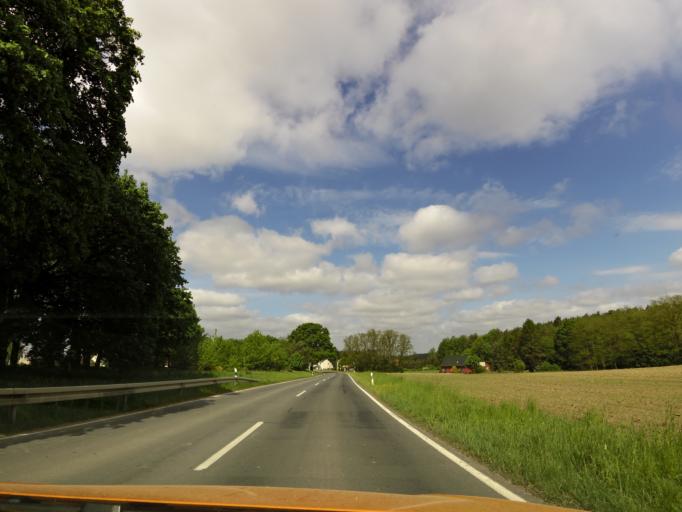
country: DE
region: Brandenburg
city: Wiesenburg
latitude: 52.1073
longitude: 12.4028
